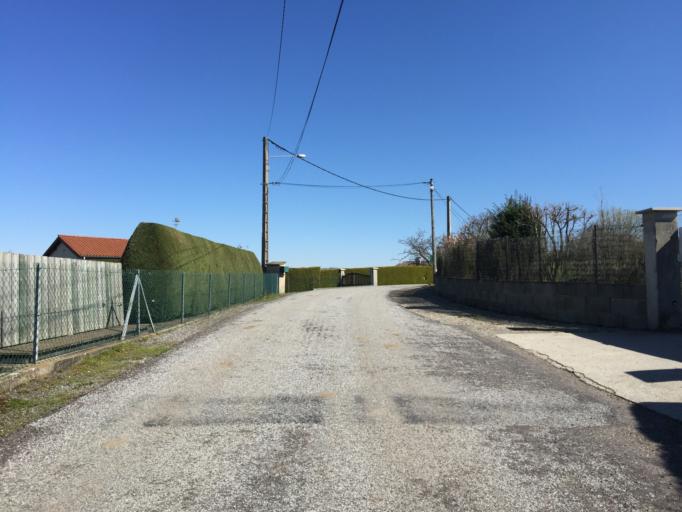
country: FR
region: Rhone-Alpes
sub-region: Departement de la Loire
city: Saint-Chamond
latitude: 45.4864
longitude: 4.4886
